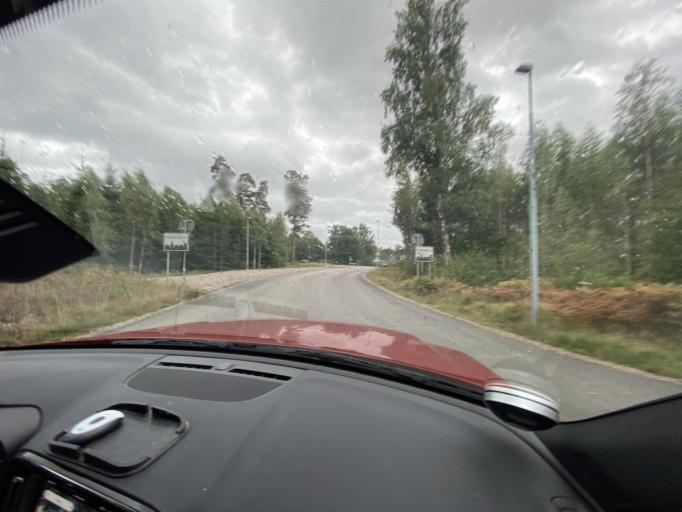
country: SE
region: Kronoberg
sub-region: Markaryds Kommun
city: Markaryd
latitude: 56.4589
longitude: 13.6170
